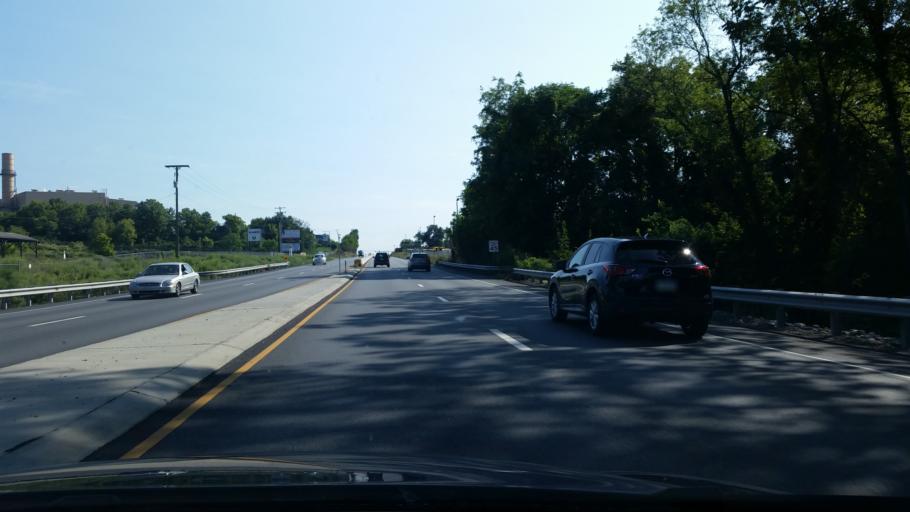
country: US
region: Pennsylvania
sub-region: Berks County
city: Temple
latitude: 40.4266
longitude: -75.9371
